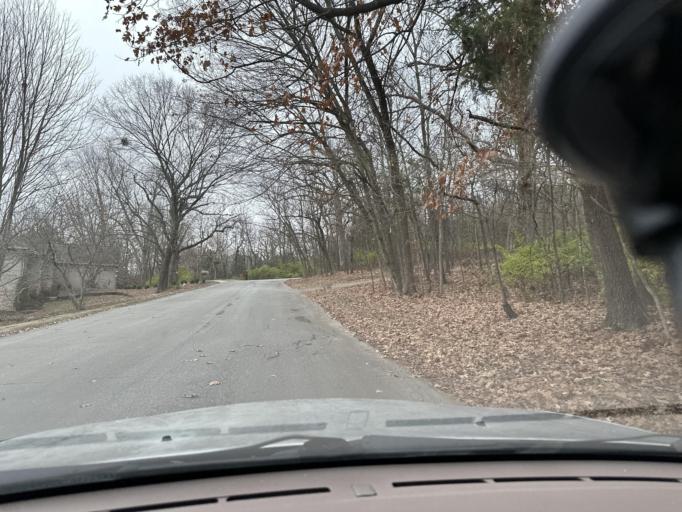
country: US
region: Arkansas
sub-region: Washington County
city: Fayetteville
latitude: 36.0820
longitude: -94.1179
